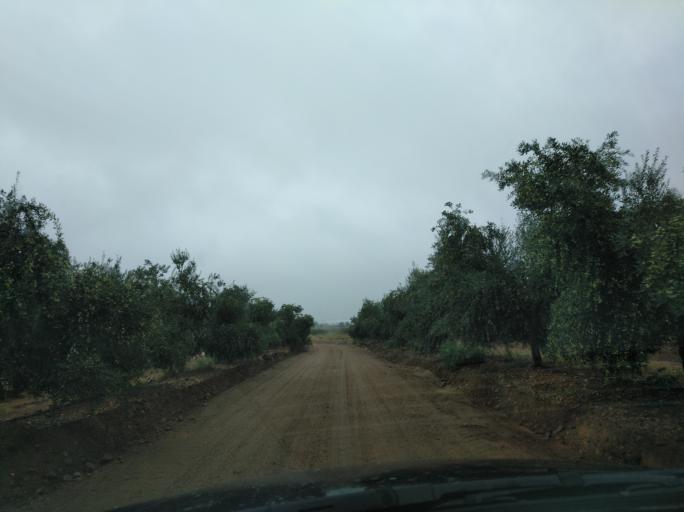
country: PT
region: Portalegre
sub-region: Campo Maior
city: Campo Maior
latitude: 38.9522
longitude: -7.0575
